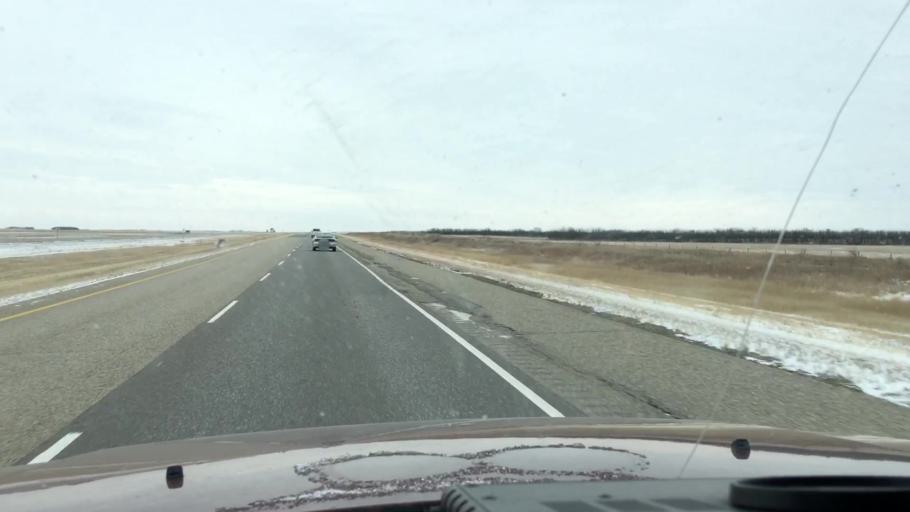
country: CA
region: Saskatchewan
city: Saskatoon
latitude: 51.4696
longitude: -106.2458
